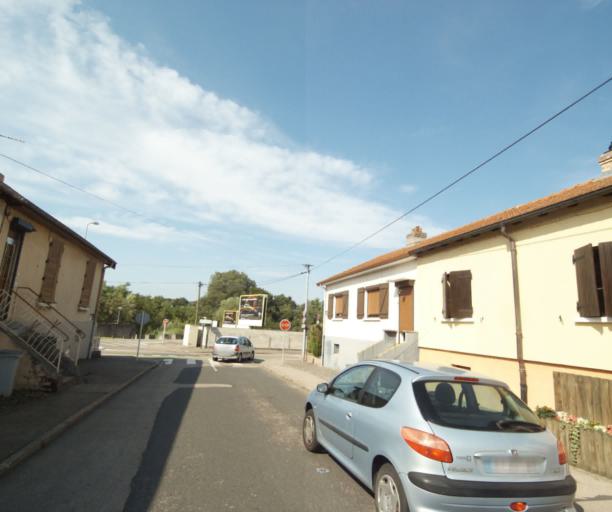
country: FR
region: Lorraine
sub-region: Departement de Meurthe-et-Moselle
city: Luneville
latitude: 48.5809
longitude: 6.5134
